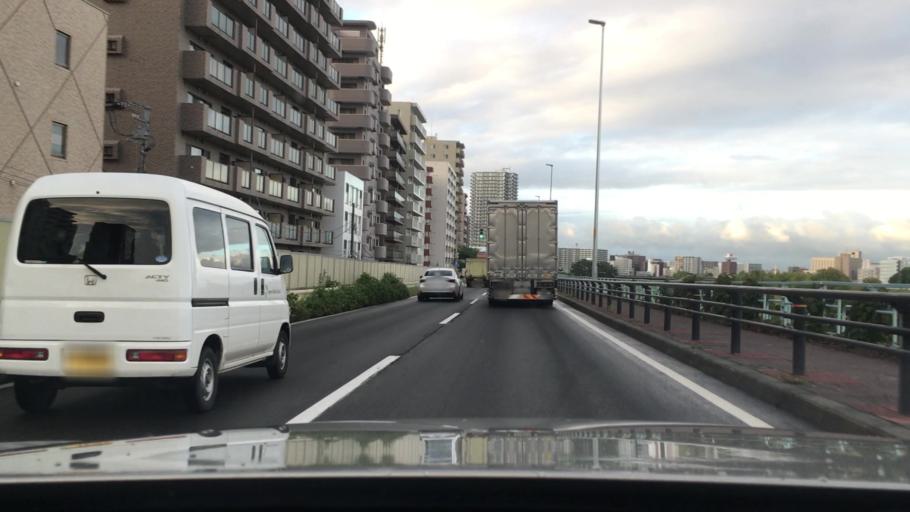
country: JP
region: Hokkaido
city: Sapporo
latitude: 43.0423
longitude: 141.3578
